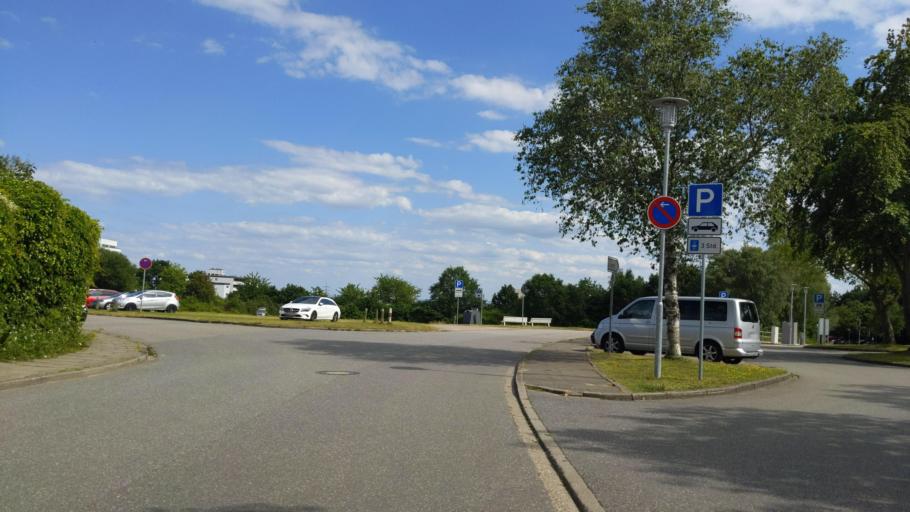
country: DE
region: Schleswig-Holstein
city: Gromitz
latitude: 54.1451
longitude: 10.9524
